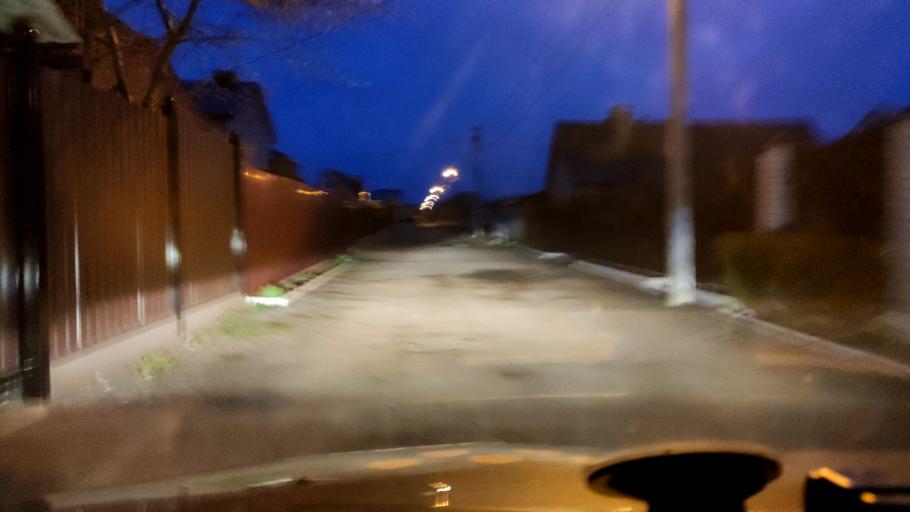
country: RU
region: Voronezj
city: Pridonskoy
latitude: 51.6333
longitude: 39.1046
